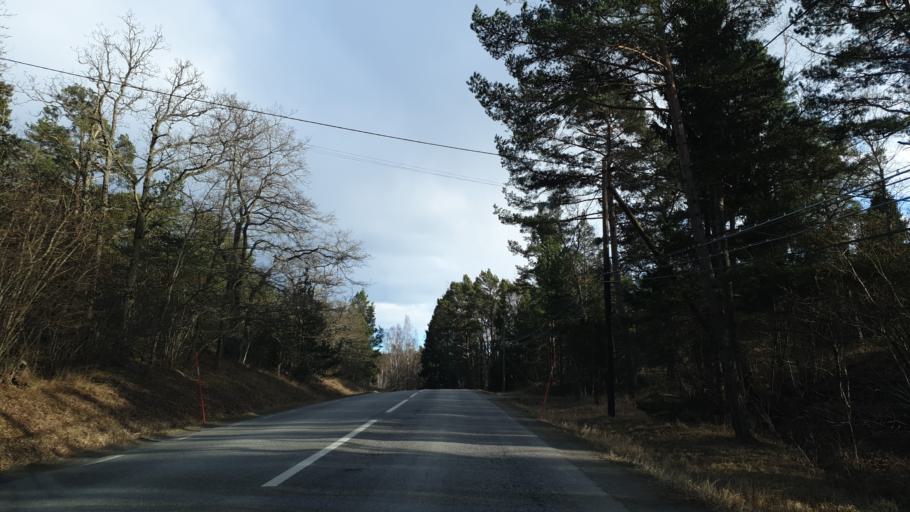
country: SE
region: Stockholm
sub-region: Varmdo Kommun
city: Holo
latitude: 59.3236
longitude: 18.7228
